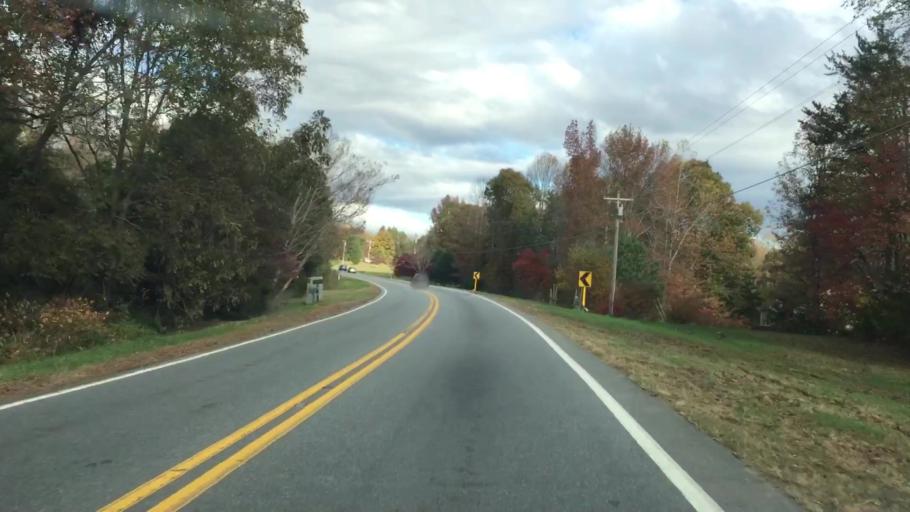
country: US
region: North Carolina
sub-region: Guilford County
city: Stokesdale
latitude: 36.2328
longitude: -80.0145
